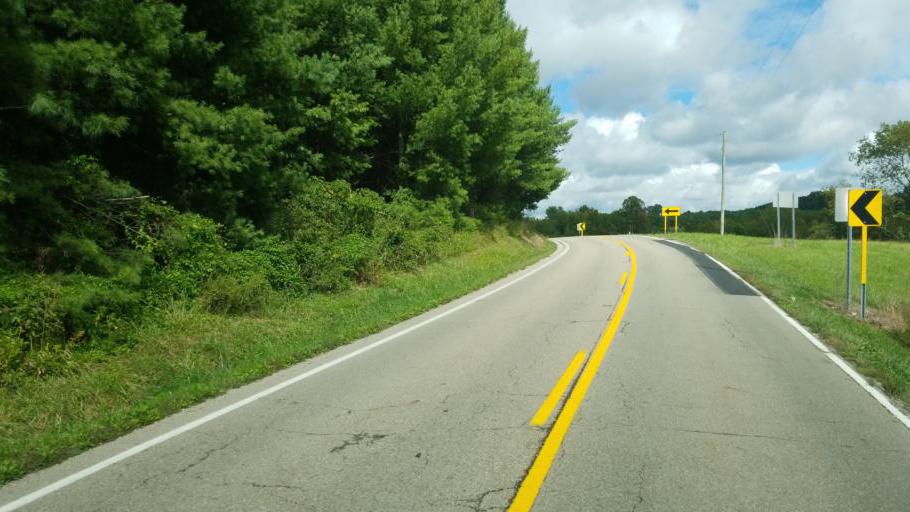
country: US
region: Ohio
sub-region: Jackson County
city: Oak Hill
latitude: 38.8810
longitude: -82.6949
